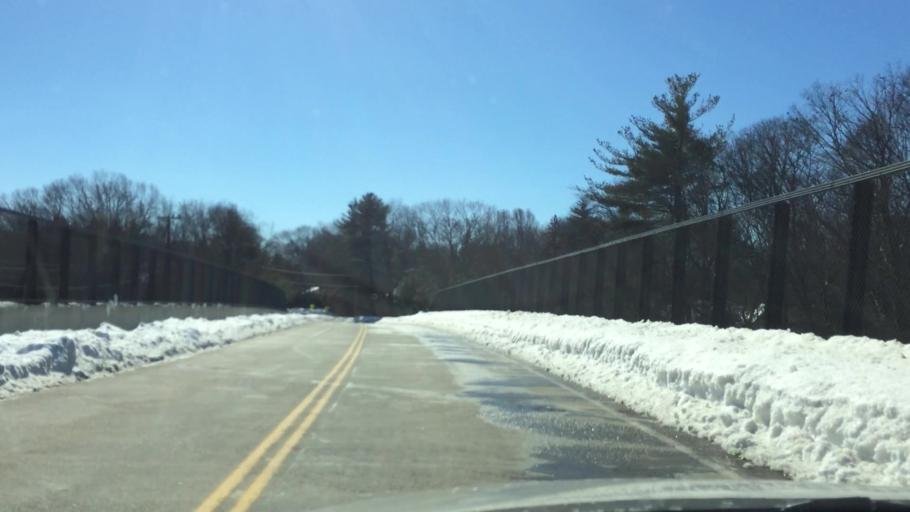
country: US
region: Massachusetts
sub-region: Middlesex County
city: Bedford
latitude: 42.5181
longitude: -71.2592
